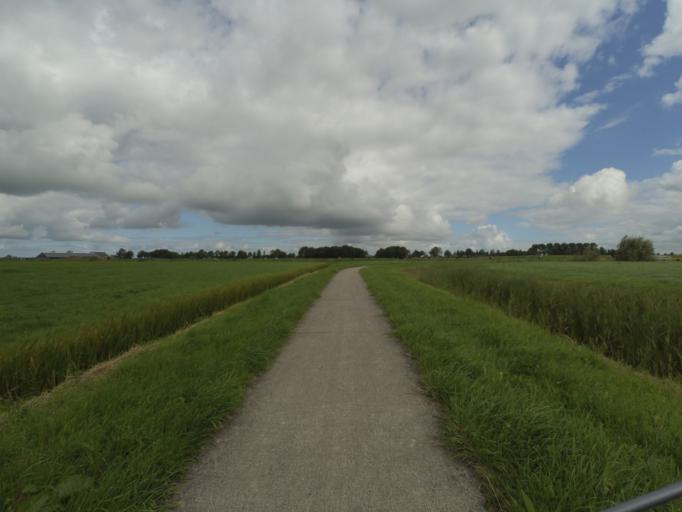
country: NL
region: Friesland
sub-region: Gemeente Kollumerland en Nieuwkruisland
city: Kollum
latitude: 53.2906
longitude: 6.2289
